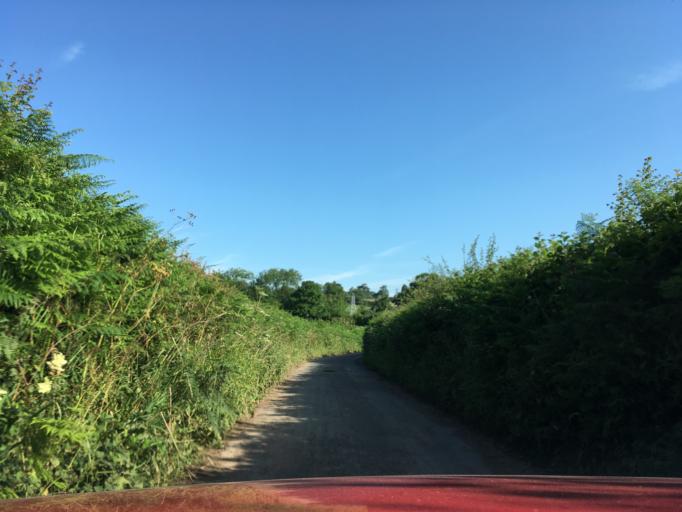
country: GB
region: England
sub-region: Gloucestershire
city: Berkeley
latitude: 51.7567
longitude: -2.4645
